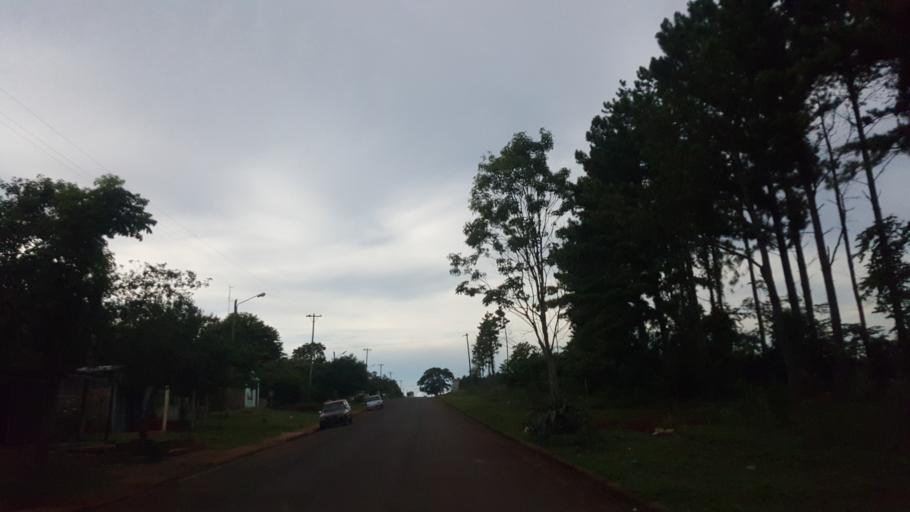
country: AR
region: Misiones
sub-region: Departamento de San Ignacio
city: San Ignacio
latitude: -27.2682
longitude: -55.5234
